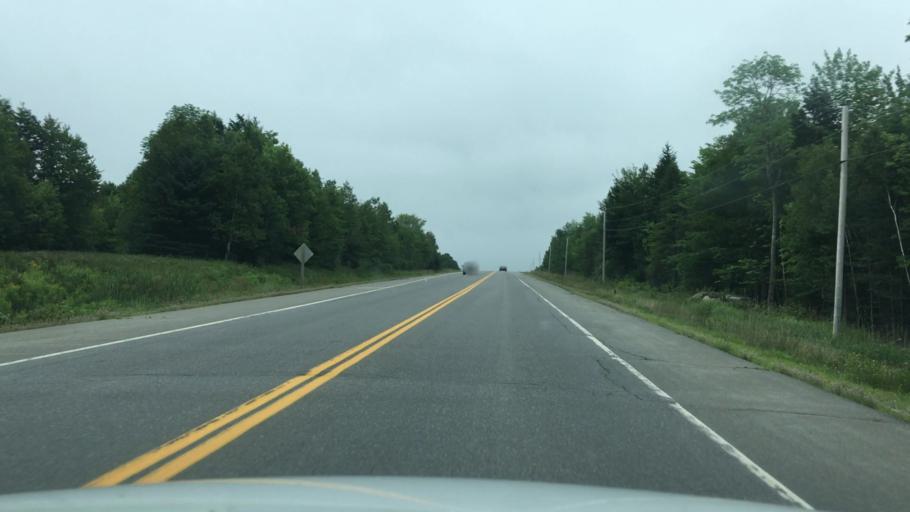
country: US
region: Maine
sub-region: Hancock County
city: Franklin
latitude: 44.8290
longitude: -68.1274
